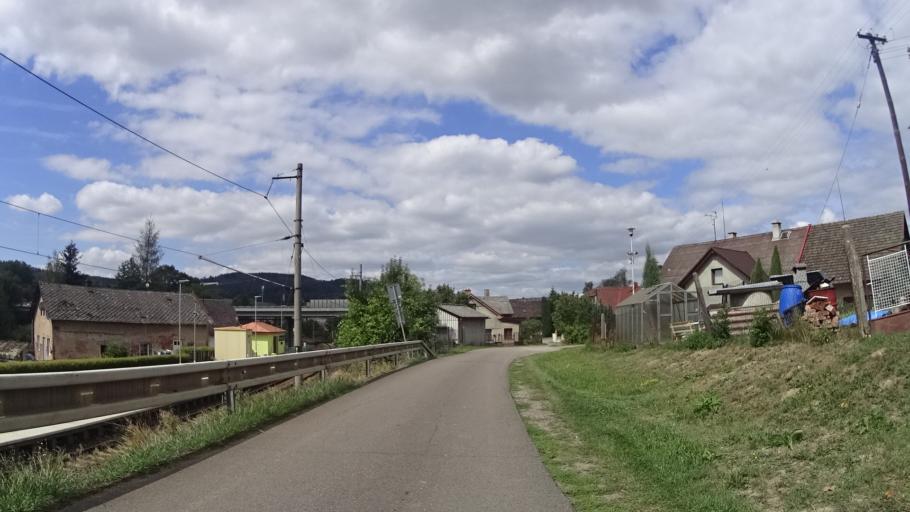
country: CZ
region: Pardubicky
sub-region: Okres Usti nad Orlici
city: Usti nad Orlici
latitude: 49.9894
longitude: 16.3980
